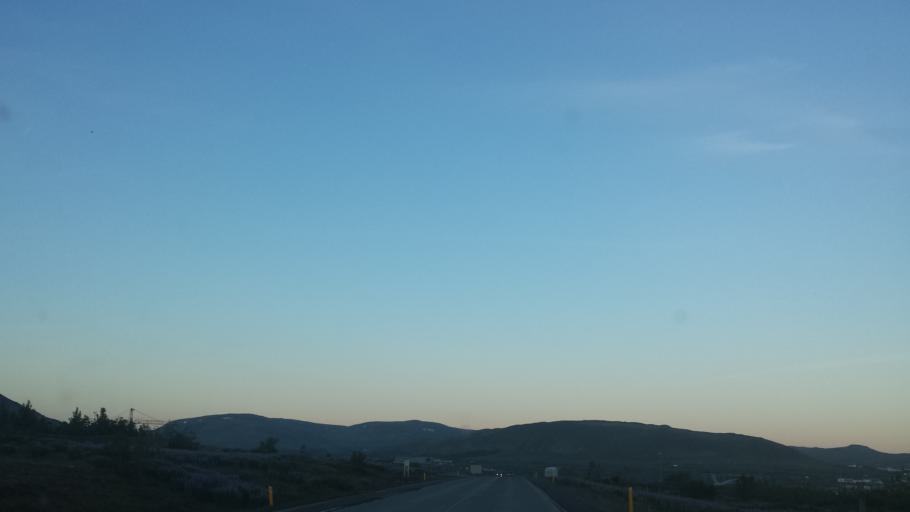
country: IS
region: Capital Region
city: Mosfellsbaer
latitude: 64.1952
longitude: -21.7004
